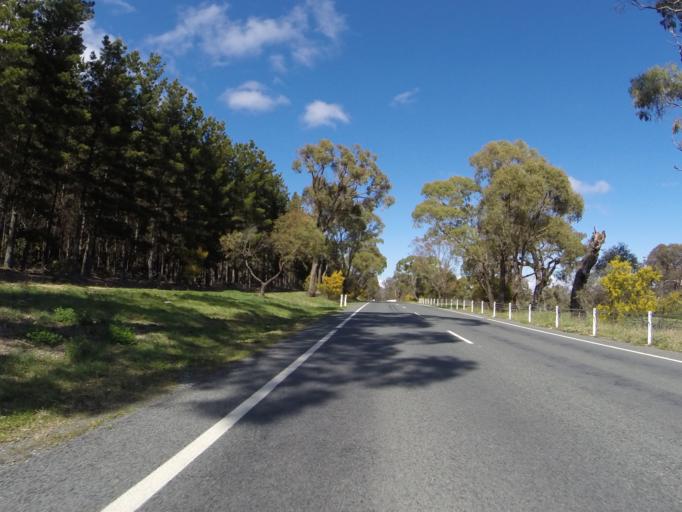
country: AU
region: New South Wales
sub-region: Queanbeyan
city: Queanbeyan
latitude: -35.2958
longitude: 149.2547
